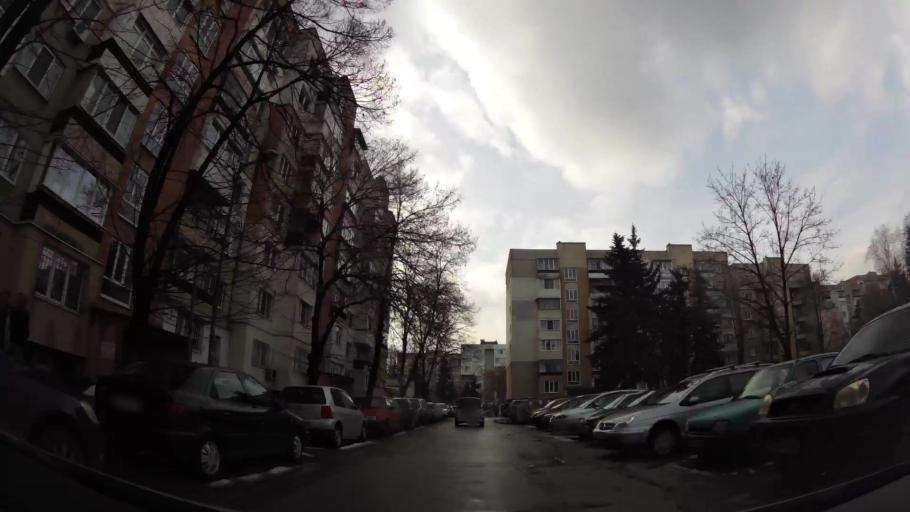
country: BG
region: Sofiya
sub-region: Obshtina Bozhurishte
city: Bozhurishte
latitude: 42.7178
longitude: 23.2502
